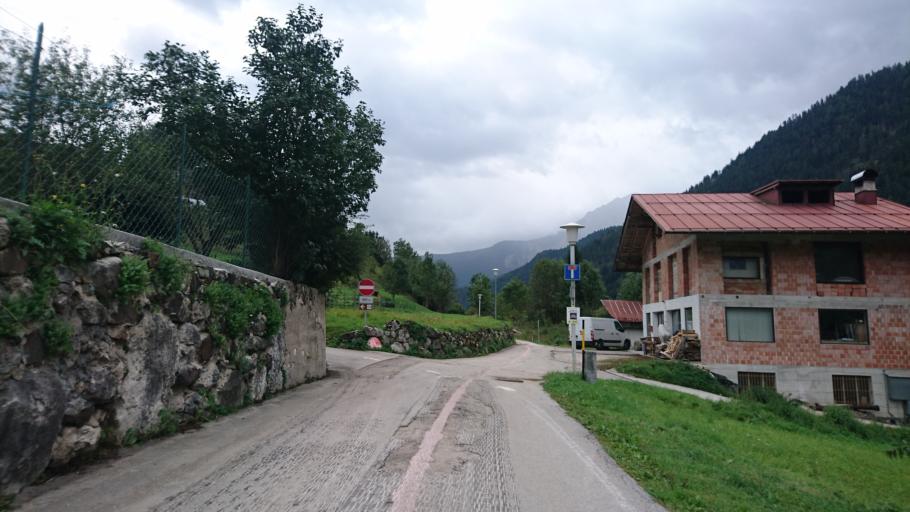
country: IT
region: Veneto
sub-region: Provincia di Belluno
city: Vodo
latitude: 46.4137
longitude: 12.2588
